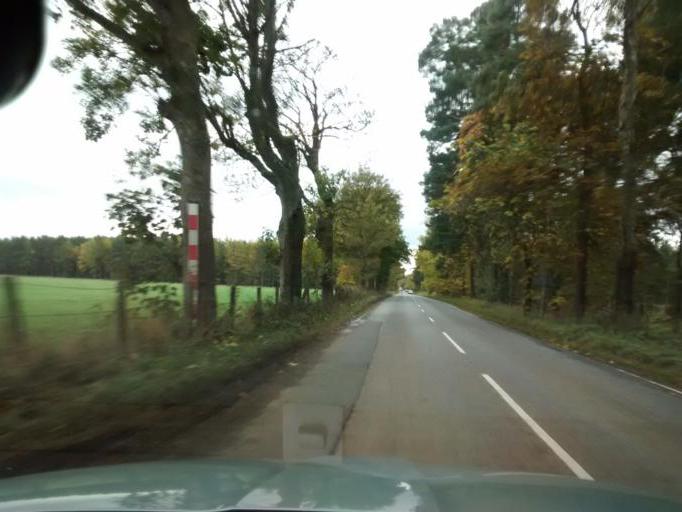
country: GB
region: Scotland
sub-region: Perth and Kinross
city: Blairgowrie
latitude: 56.5510
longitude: -3.3511
